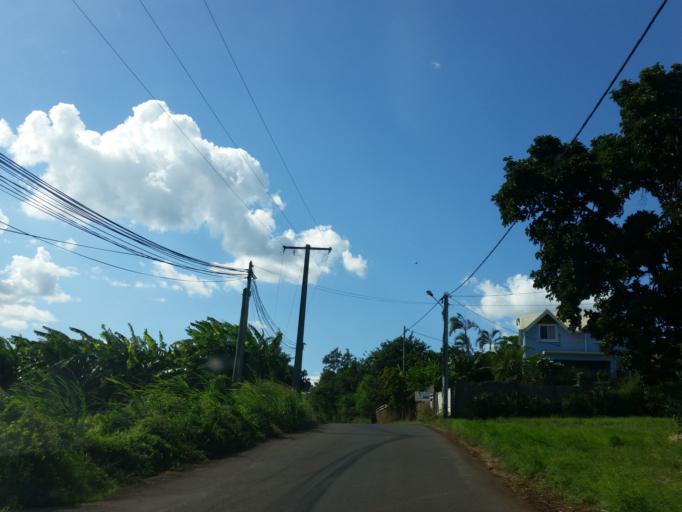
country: RE
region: Reunion
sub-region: Reunion
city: Saint-Pierre
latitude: -21.3220
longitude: 55.5014
